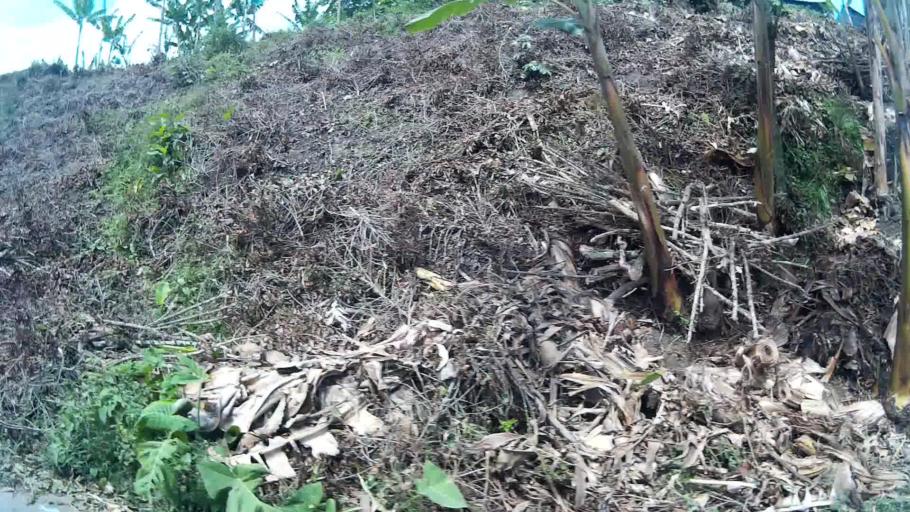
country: CO
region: Caldas
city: Belalcazar
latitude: 4.9742
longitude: -75.8182
